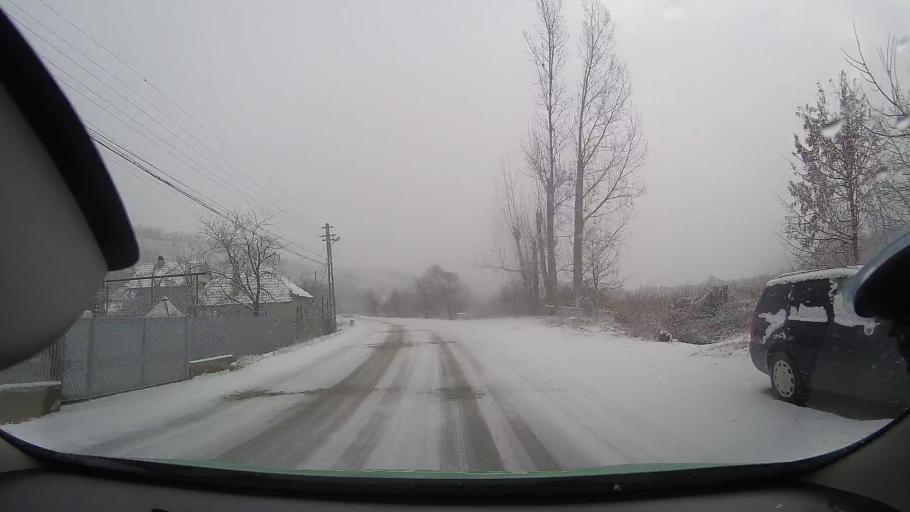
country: RO
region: Alba
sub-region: Comuna Livezile
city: Livezile
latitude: 46.3417
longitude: 23.6630
